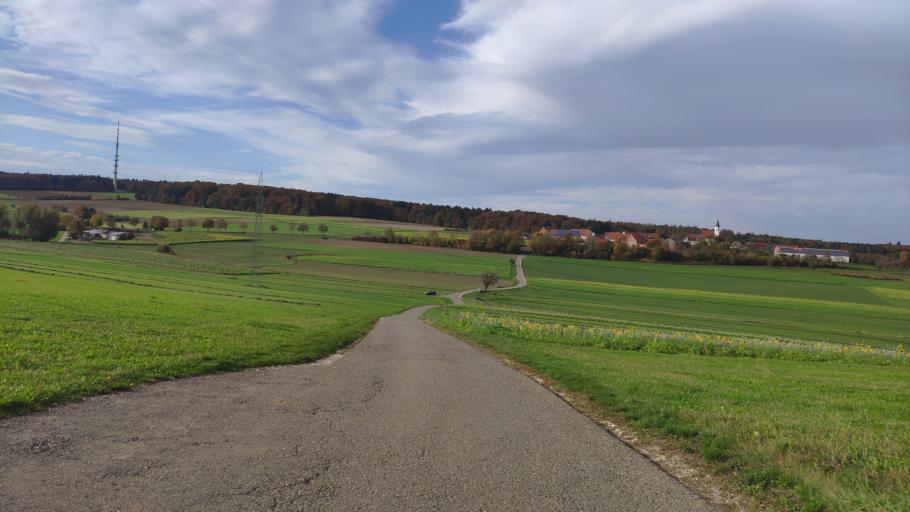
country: DE
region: Baden-Wuerttemberg
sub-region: Tuebingen Region
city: Erbach
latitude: 48.3841
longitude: 9.9180
